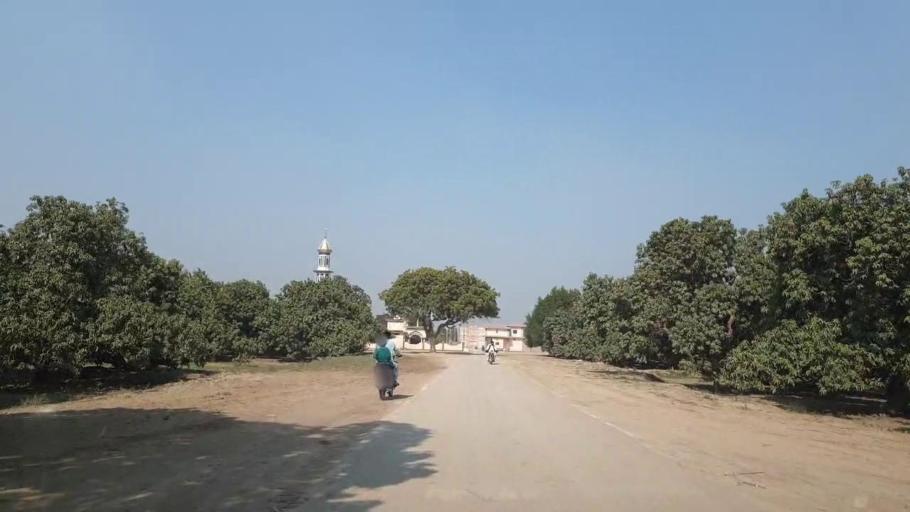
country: PK
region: Sindh
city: Tando Allahyar
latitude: 25.4907
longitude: 68.8225
